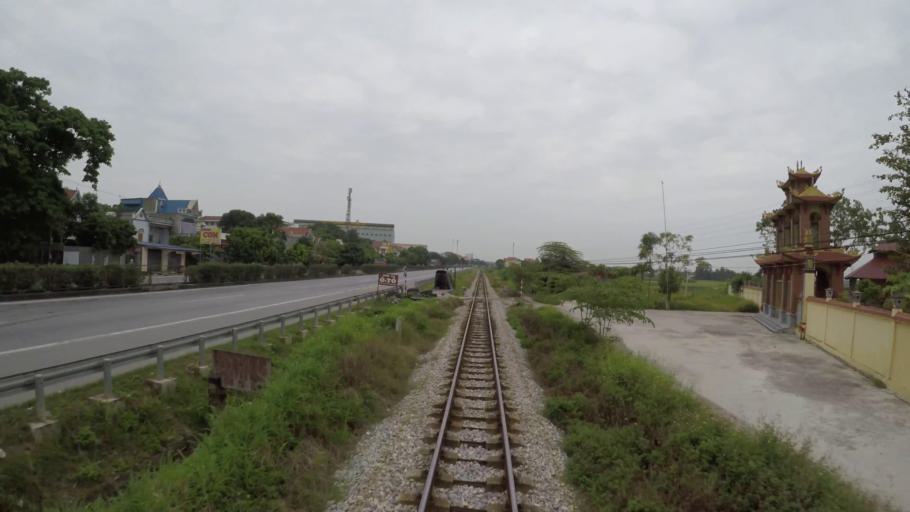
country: VN
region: Hai Duong
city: Phu Thai
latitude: 20.9442
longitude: 106.5428
